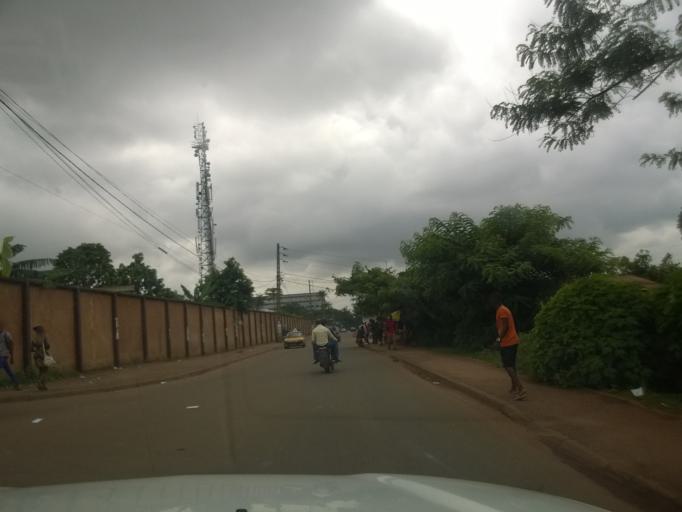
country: CM
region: Centre
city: Yaounde
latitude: 3.8546
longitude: 11.5078
